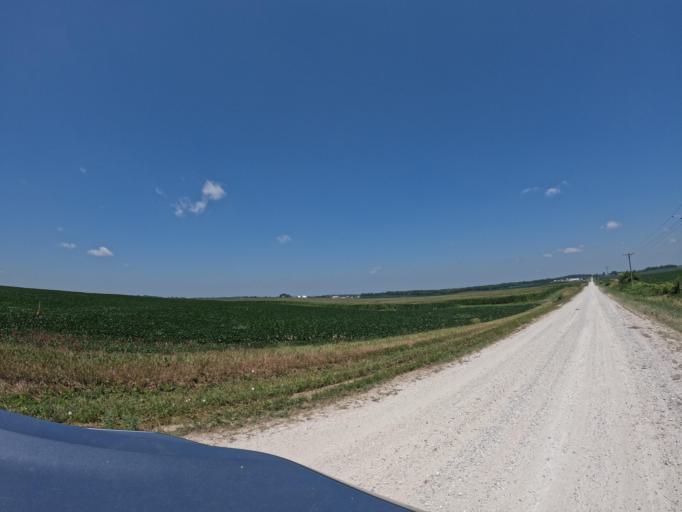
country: US
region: Iowa
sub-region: Keokuk County
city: Sigourney
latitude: 41.2825
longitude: -92.2189
